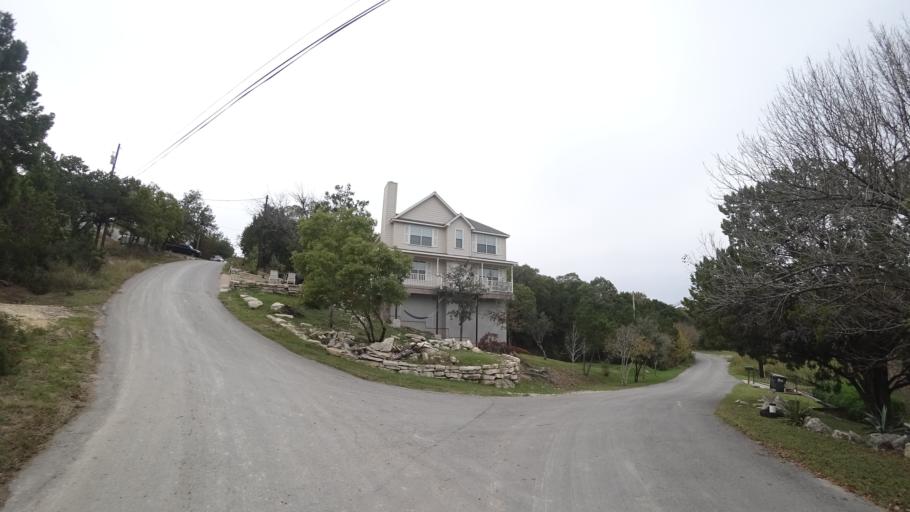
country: US
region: Texas
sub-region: Travis County
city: Hudson Bend
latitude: 30.3787
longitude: -97.9248
